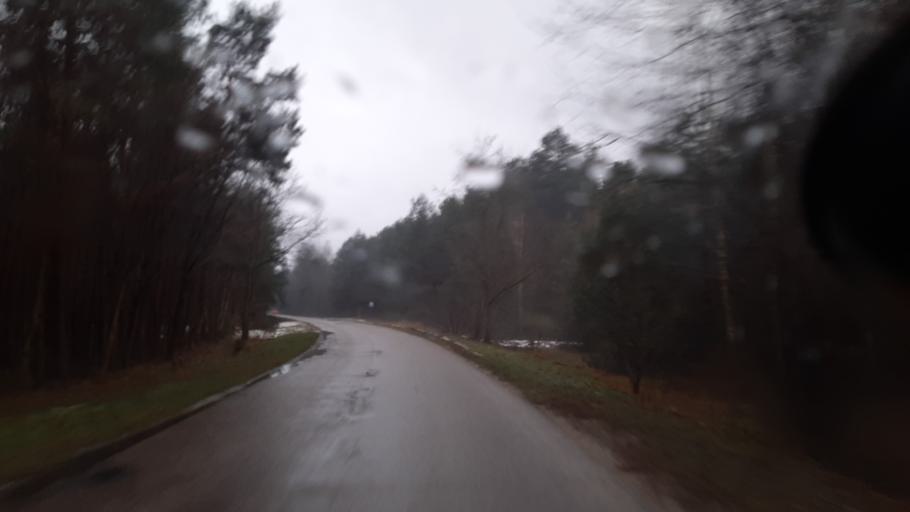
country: PL
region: Lublin Voivodeship
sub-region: Powiat lubartowski
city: Kamionka
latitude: 51.5109
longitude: 22.4911
